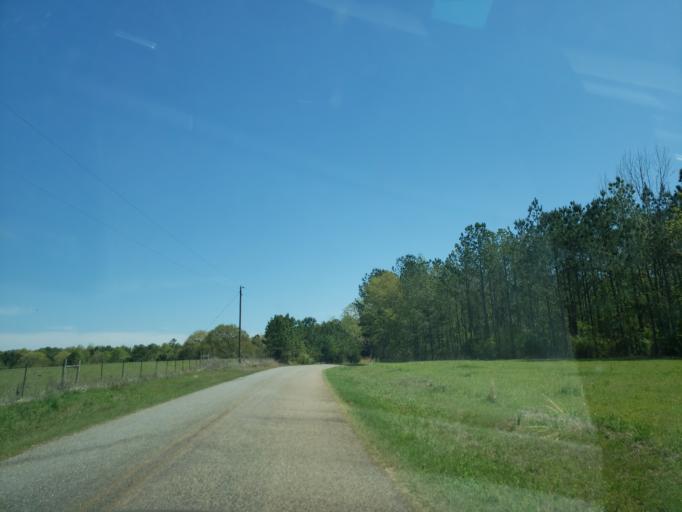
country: US
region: Alabama
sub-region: Tallapoosa County
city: Camp Hill
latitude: 32.6714
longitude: -85.7459
